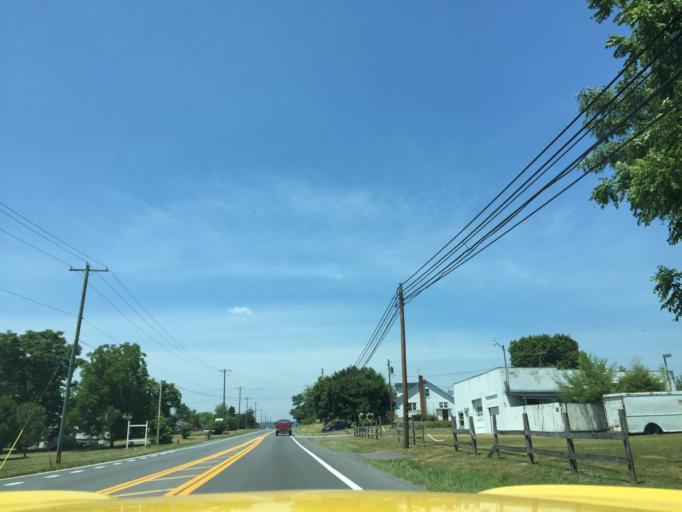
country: US
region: West Virginia
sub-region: Berkeley County
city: Inwood
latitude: 39.3466
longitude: -78.0240
